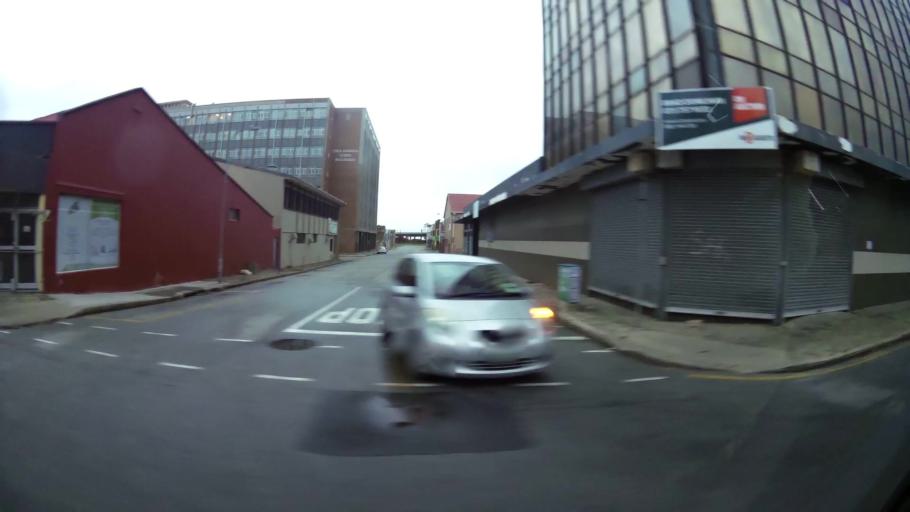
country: ZA
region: Eastern Cape
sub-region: Nelson Mandela Bay Metropolitan Municipality
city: Port Elizabeth
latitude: -33.9452
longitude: 25.6062
